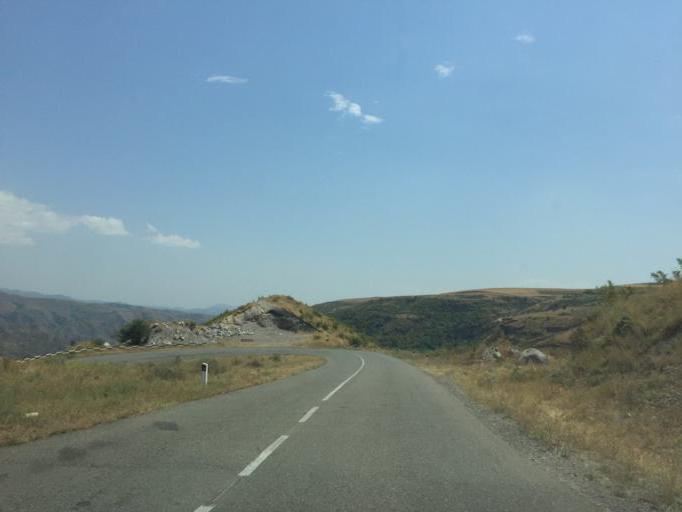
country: AZ
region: Lacin
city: Lacin
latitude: 39.5755
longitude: 46.5445
